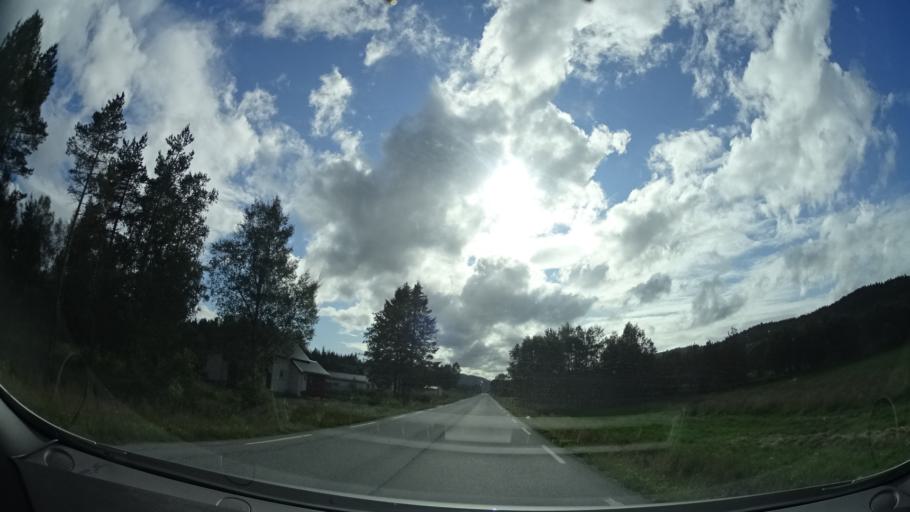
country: NO
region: More og Romsdal
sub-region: Halsa
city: Liaboen
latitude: 63.1237
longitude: 8.3388
